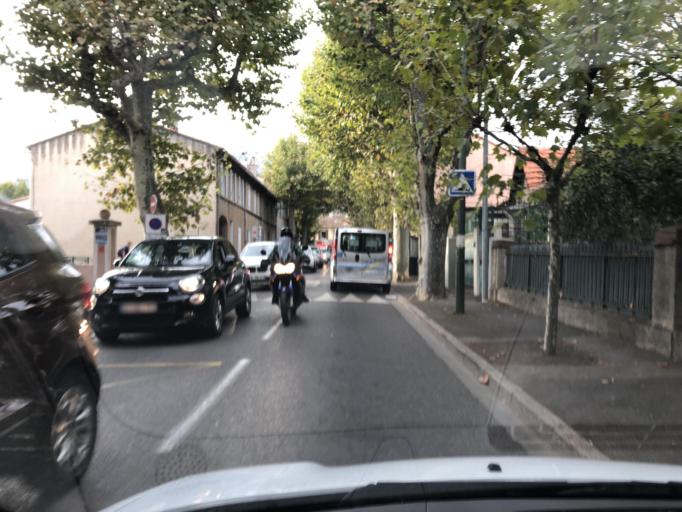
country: FR
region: Provence-Alpes-Cote d'Azur
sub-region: Departement des Bouches-du-Rhone
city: La Penne-sur-Huveaune
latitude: 43.2827
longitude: 5.5150
